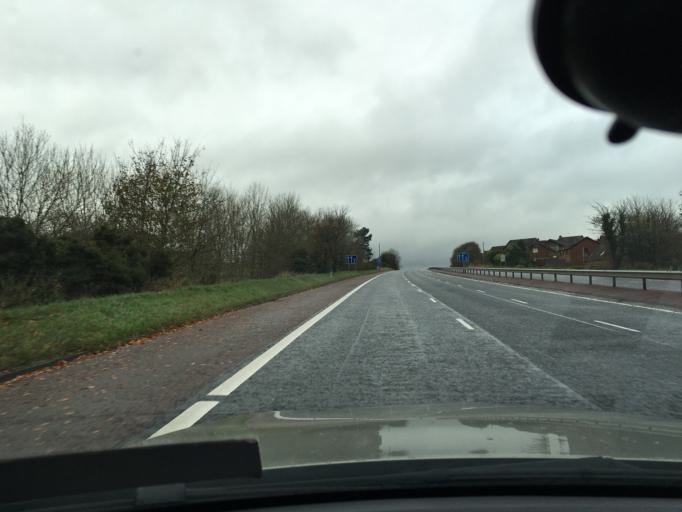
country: GB
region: Northern Ireland
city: Carnmoney
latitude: 54.6839
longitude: -5.9761
